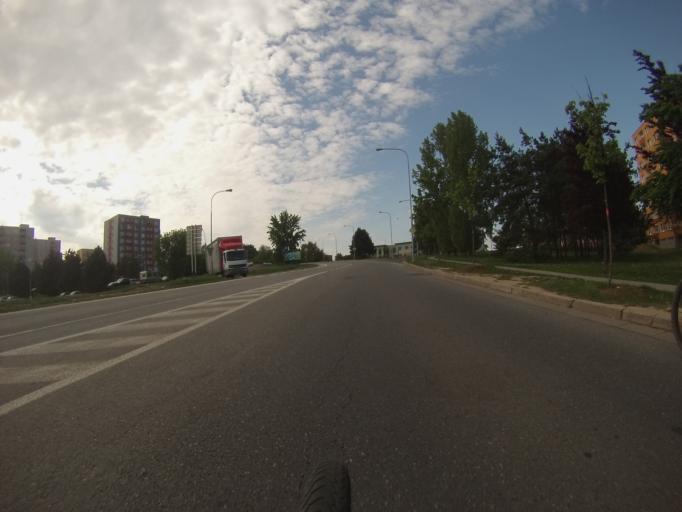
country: CZ
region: South Moravian
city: Troubsko
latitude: 49.2194
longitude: 16.5080
